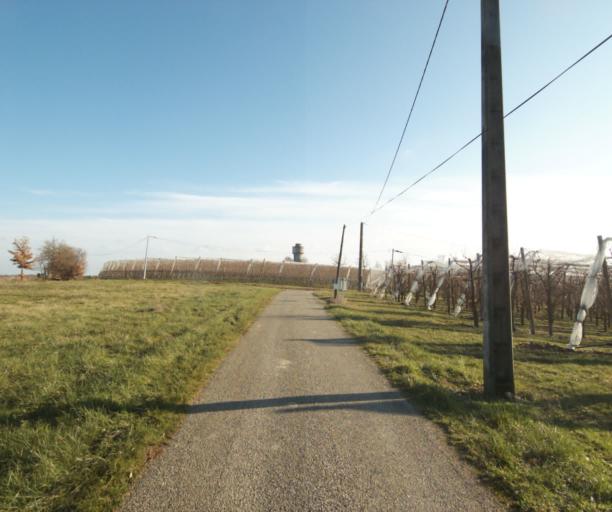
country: FR
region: Midi-Pyrenees
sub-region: Departement du Tarn-et-Garonne
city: Moissac
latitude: 44.1451
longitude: 1.0527
